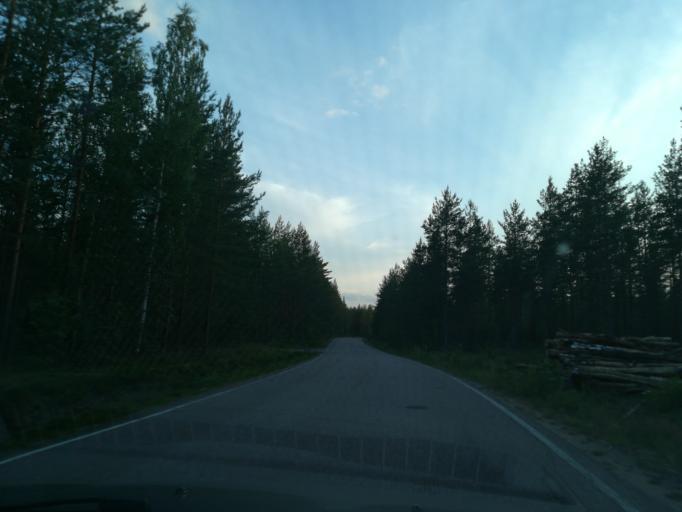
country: FI
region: South Karelia
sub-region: Lappeenranta
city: Joutseno
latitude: 61.3449
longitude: 28.4123
